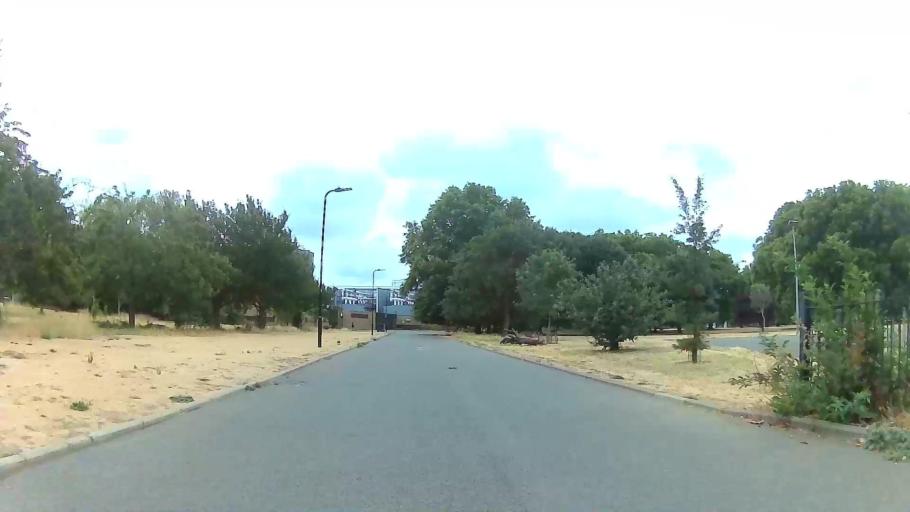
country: GB
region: England
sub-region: Greater London
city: Hackney
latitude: 51.5600
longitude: -0.0460
